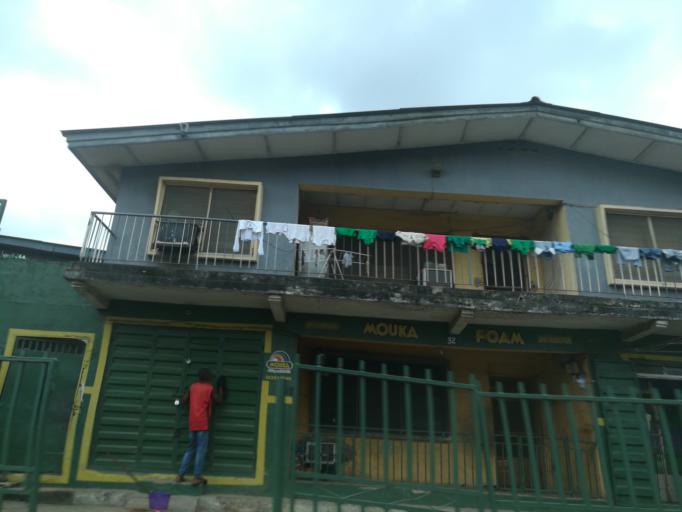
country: NG
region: Lagos
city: Oshodi
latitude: 6.5566
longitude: 3.3353
